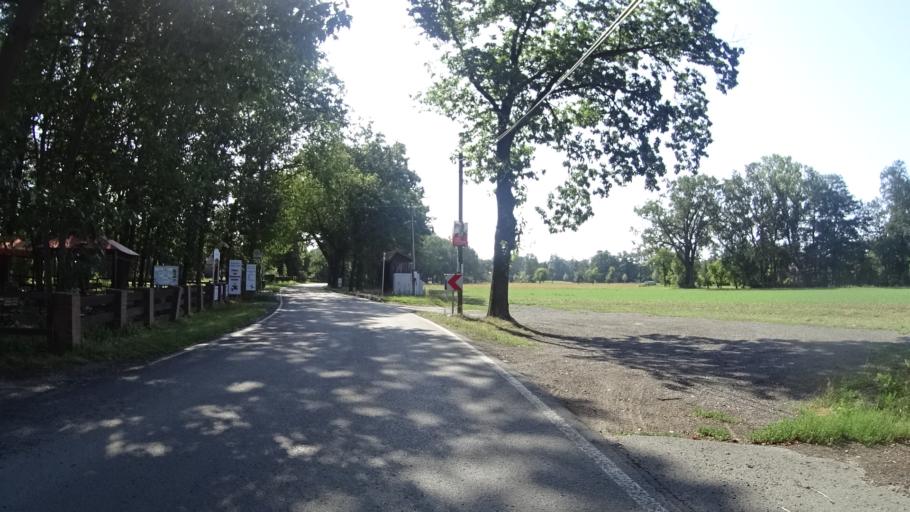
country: DE
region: Brandenburg
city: Burg
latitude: 51.8486
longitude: 14.1381
